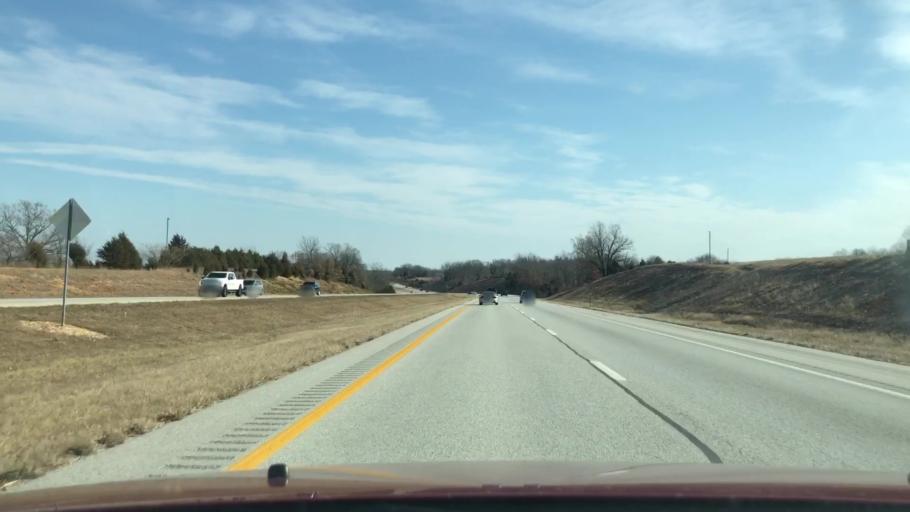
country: US
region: Missouri
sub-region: Webster County
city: Seymour
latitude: 37.1605
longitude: -92.8991
